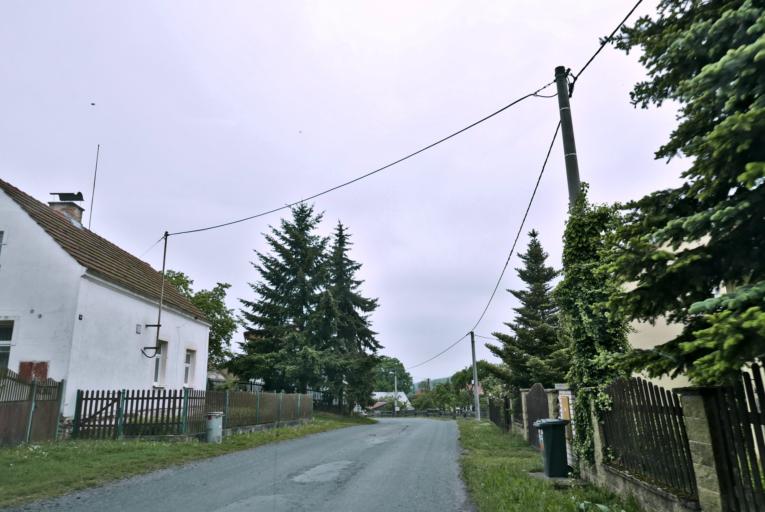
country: CZ
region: Plzensky
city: Zihle
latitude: 50.0290
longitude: 13.3248
